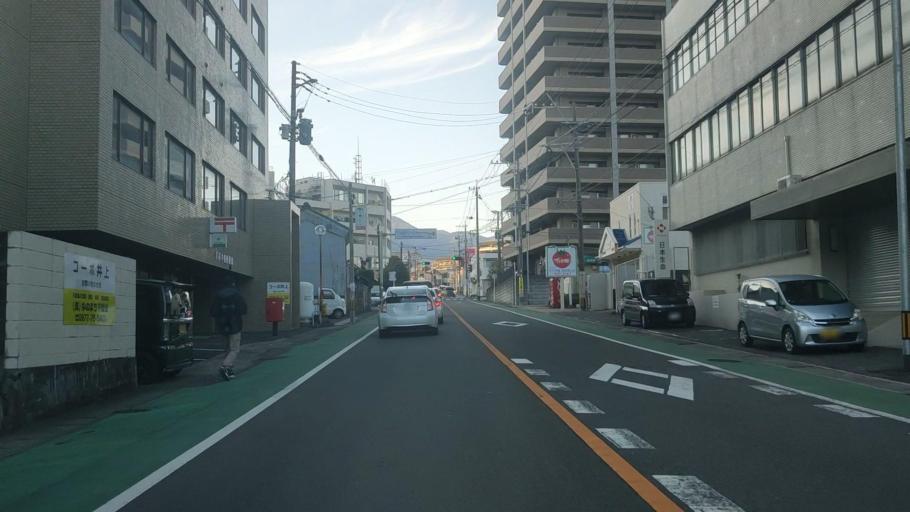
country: JP
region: Oita
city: Beppu
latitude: 33.2763
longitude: 131.4917
